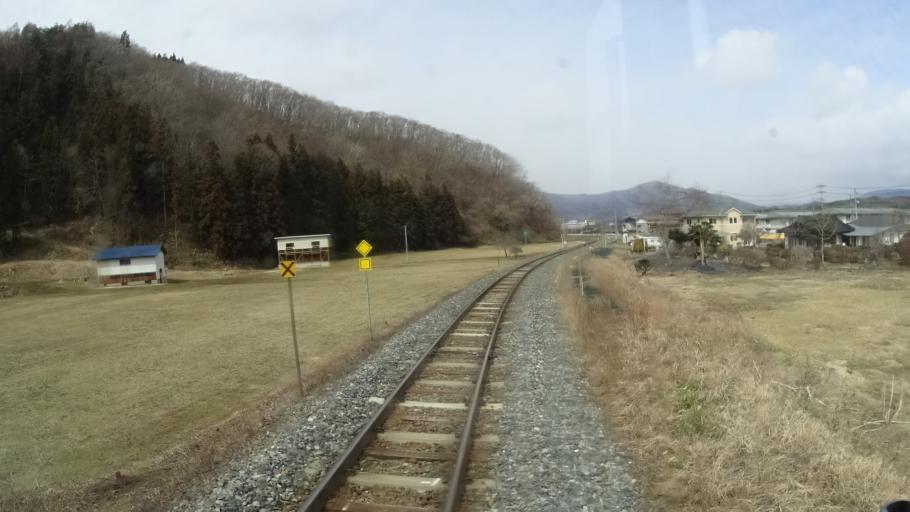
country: JP
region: Iwate
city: Tono
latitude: 39.3279
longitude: 141.5497
